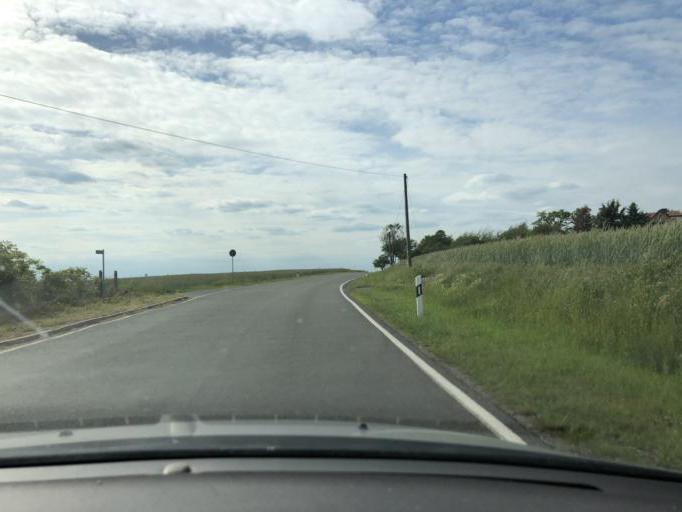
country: DE
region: Saxony
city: Grimma
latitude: 51.2785
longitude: 12.7041
